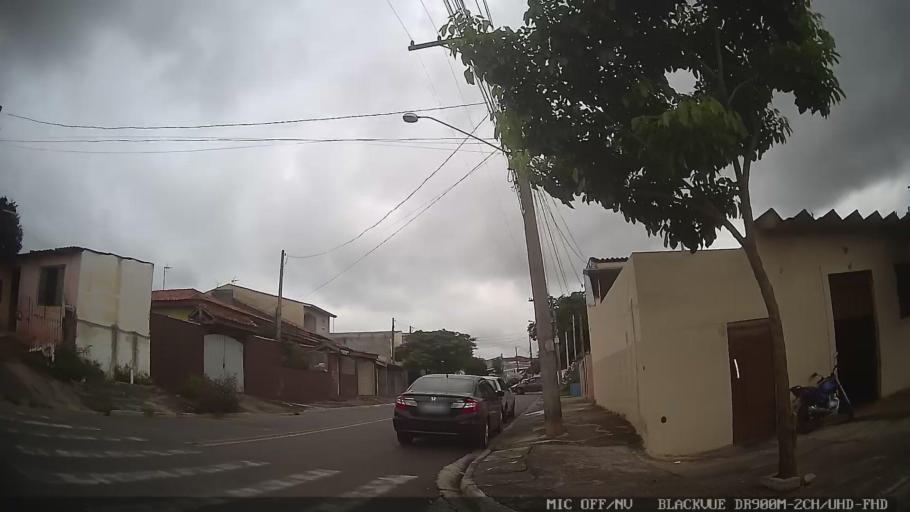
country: BR
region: Sao Paulo
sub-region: Atibaia
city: Atibaia
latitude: -23.1312
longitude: -46.5815
